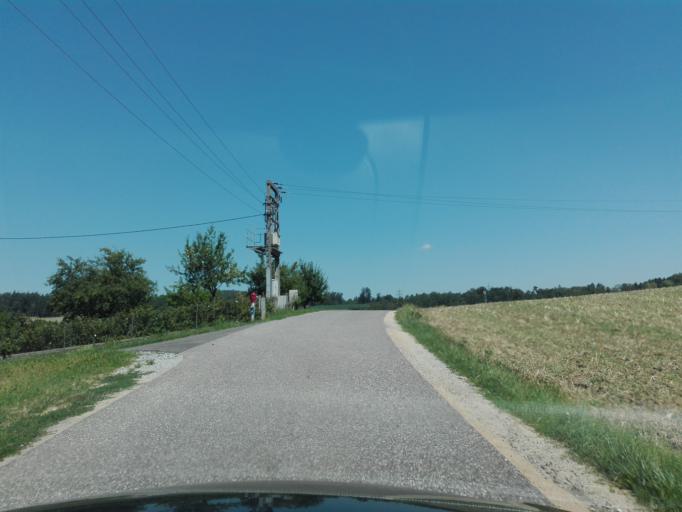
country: AT
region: Upper Austria
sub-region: Politischer Bezirk Urfahr-Umgebung
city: Gallneukirchen
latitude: 48.3154
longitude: 14.4151
